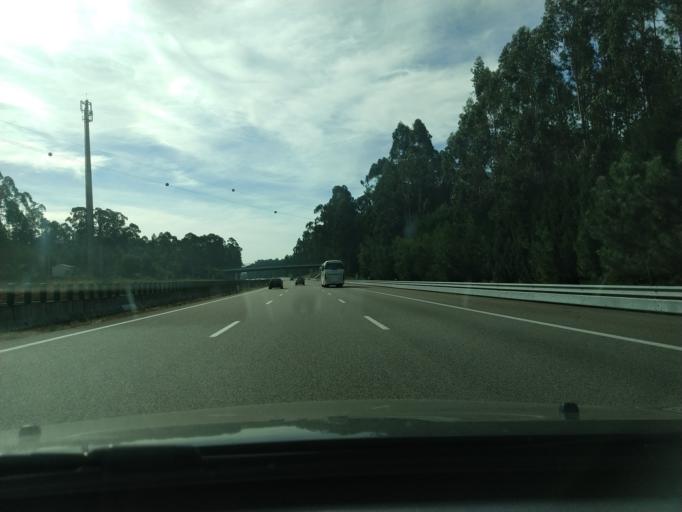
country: PT
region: Aveiro
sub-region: Ovar
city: Valega
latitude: 40.8292
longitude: -8.5544
